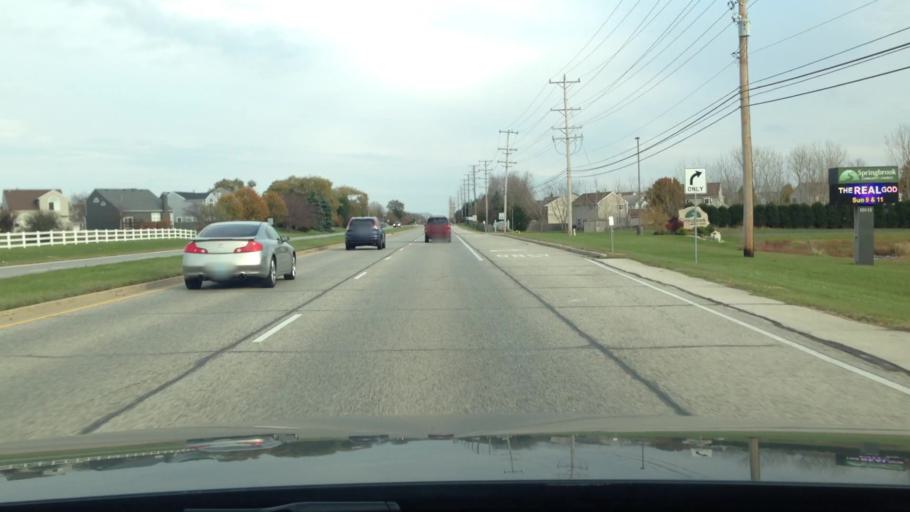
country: US
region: Illinois
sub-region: McHenry County
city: Huntley
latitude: 42.1756
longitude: -88.3948
